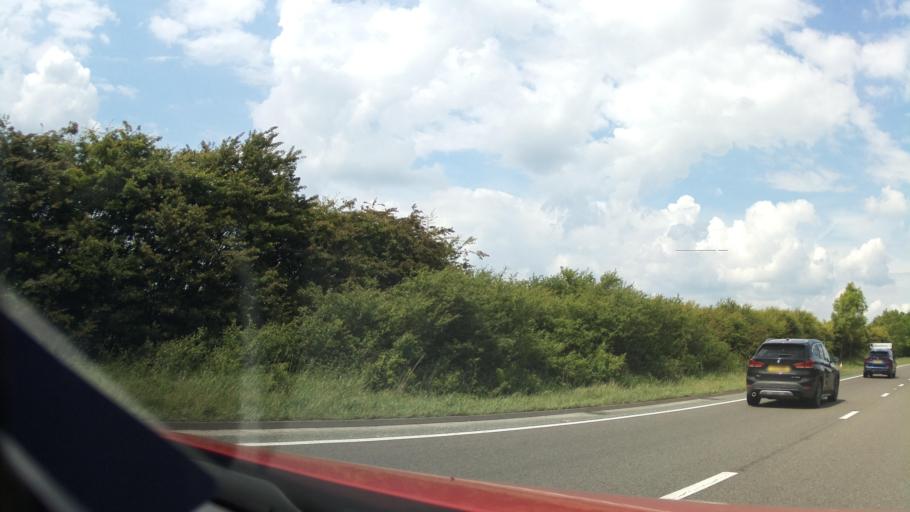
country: GB
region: England
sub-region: North Yorkshire
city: Northallerton
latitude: 54.3632
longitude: -1.3238
